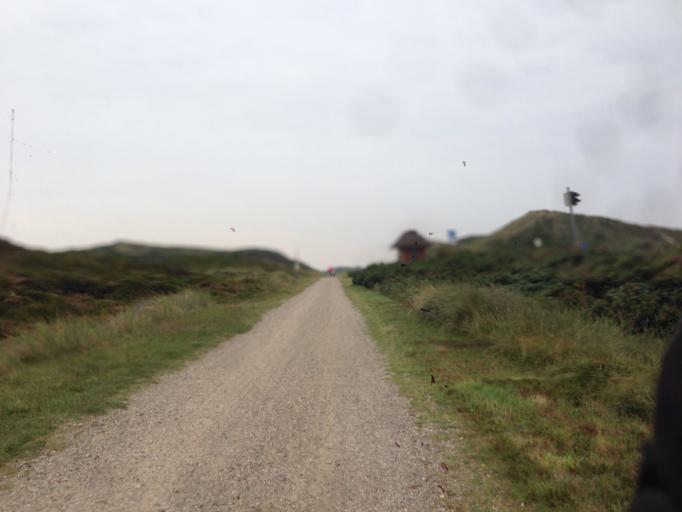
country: DE
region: Schleswig-Holstein
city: Westerland
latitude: 54.8155
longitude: 8.2914
